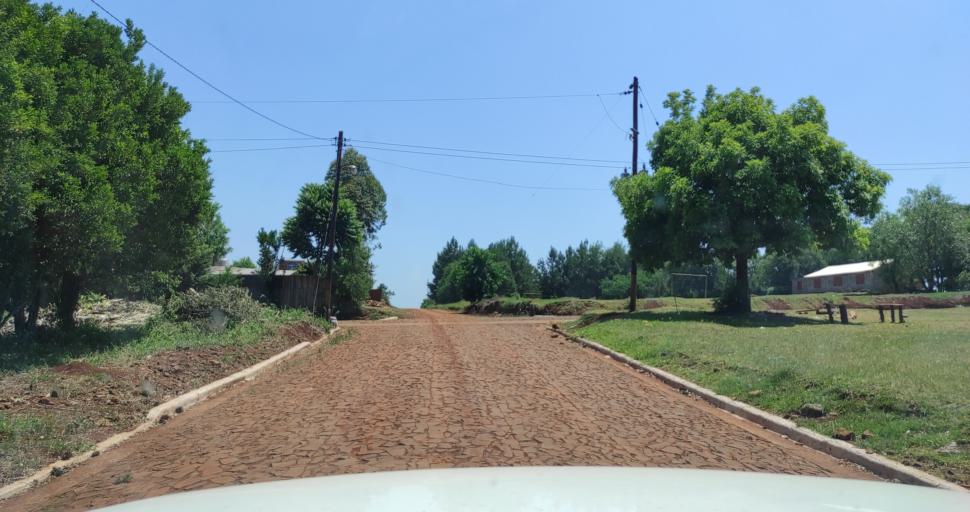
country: AR
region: Misiones
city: Santo Pipo
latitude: -27.1090
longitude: -55.3444
